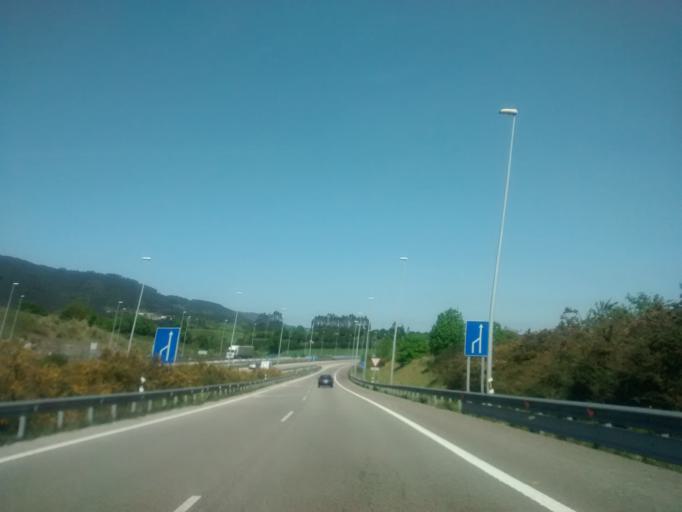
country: ES
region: Asturias
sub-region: Province of Asturias
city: Villaviciosa
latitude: 43.4653
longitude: -5.4853
